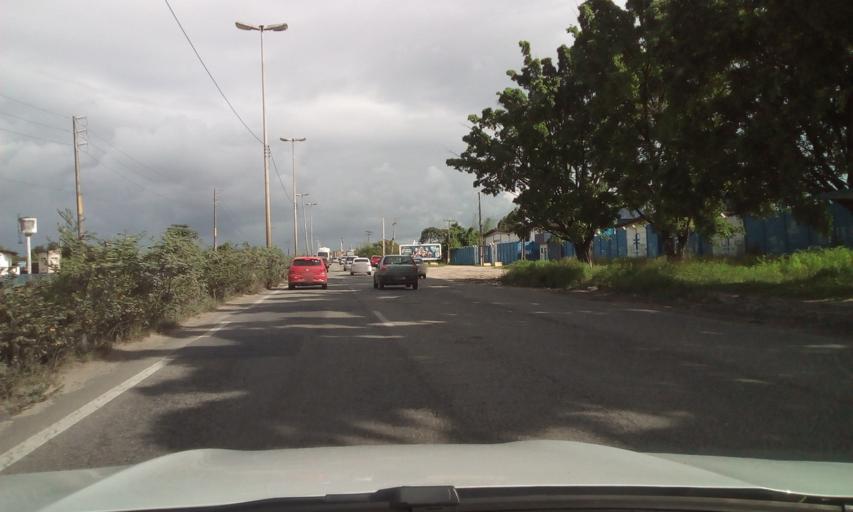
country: BR
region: Pernambuco
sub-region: Recife
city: Recife
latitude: -8.0215
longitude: -34.9427
